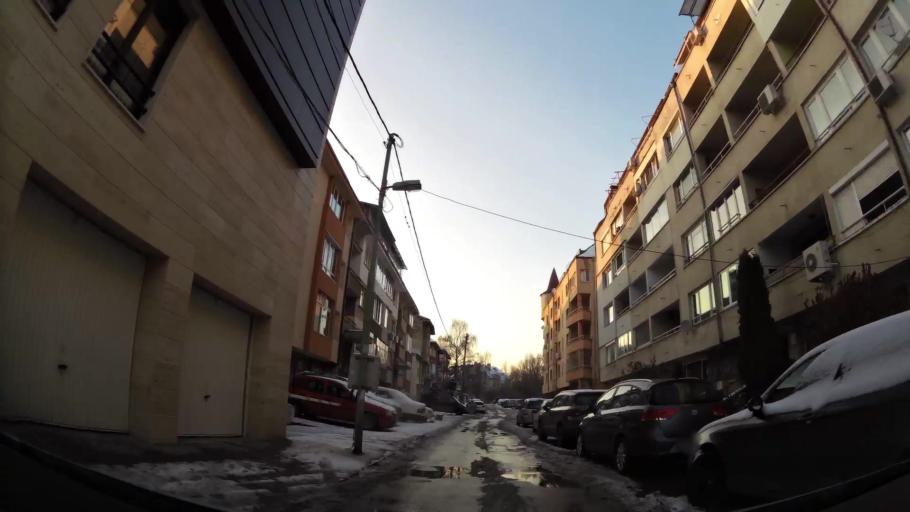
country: BG
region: Sofia-Capital
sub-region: Stolichna Obshtina
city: Sofia
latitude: 42.6863
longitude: 23.3596
